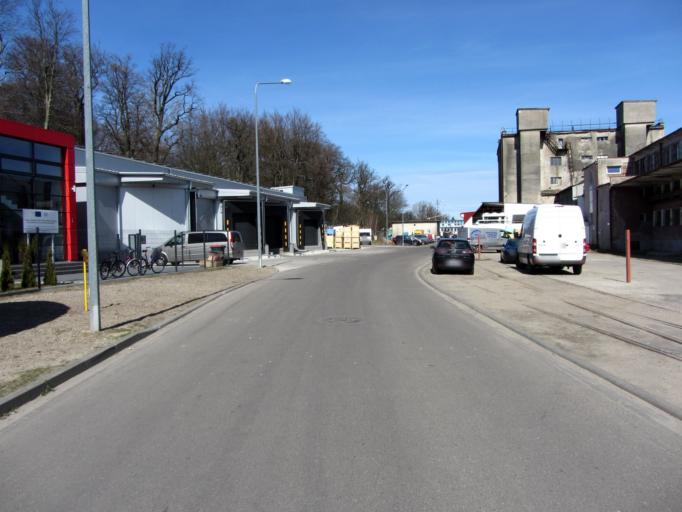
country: PL
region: West Pomeranian Voivodeship
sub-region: Powiat kolobrzeski
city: Kolobrzeg
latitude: 54.1793
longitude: 15.5506
